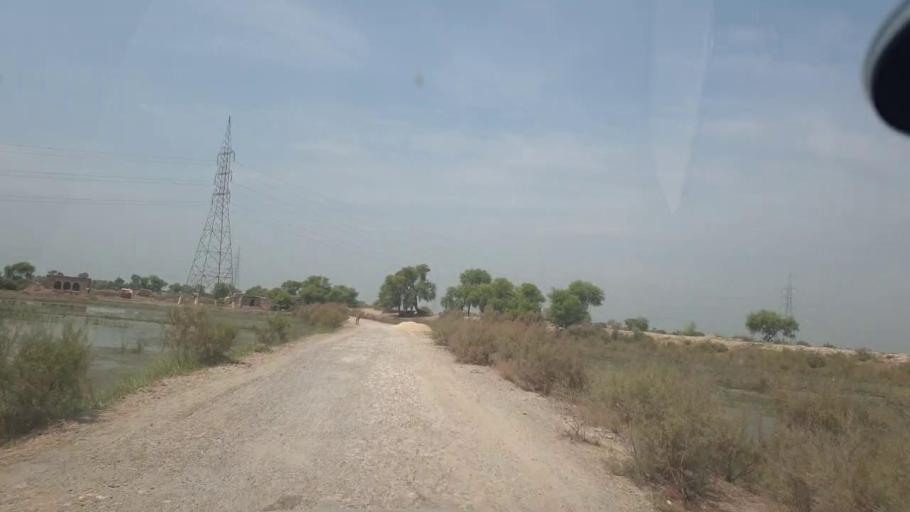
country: PK
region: Sindh
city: Thul
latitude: 28.1810
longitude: 68.6162
